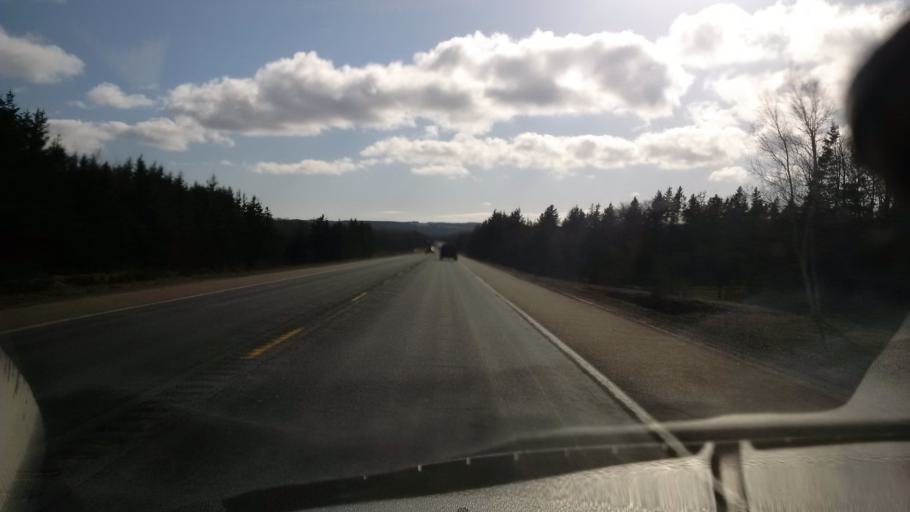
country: CA
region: Nova Scotia
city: Antigonish
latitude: 45.5802
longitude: -62.0982
